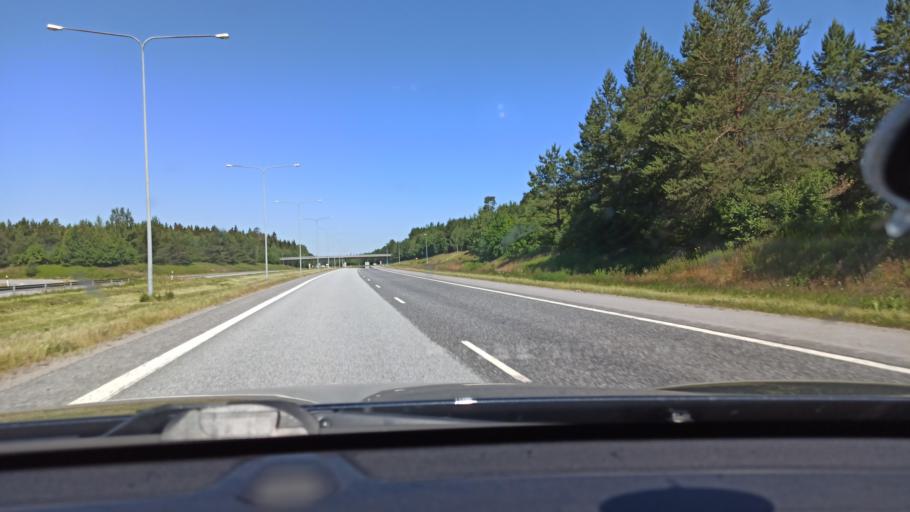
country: FI
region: Ostrobothnia
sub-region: Vaasa
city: Ristinummi
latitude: 63.0543
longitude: 21.7139
